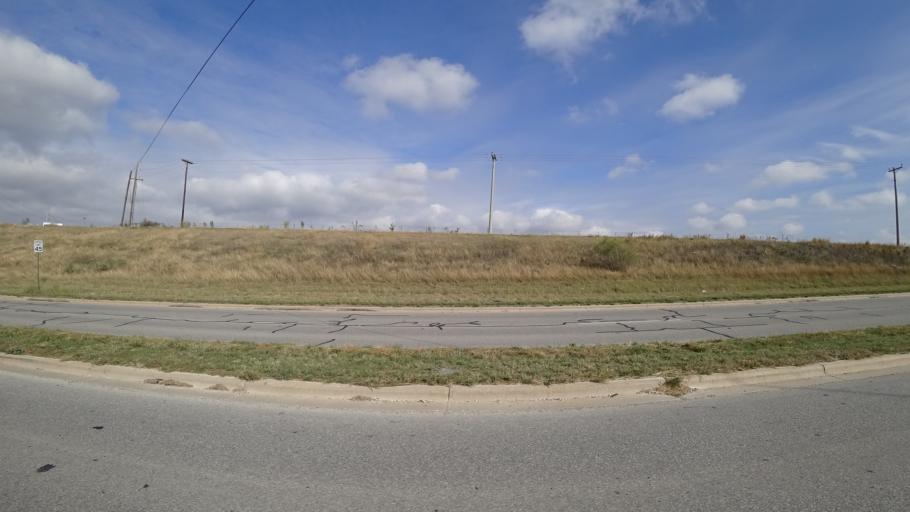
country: US
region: Texas
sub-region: Travis County
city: Wells Branch
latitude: 30.4489
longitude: -97.7175
